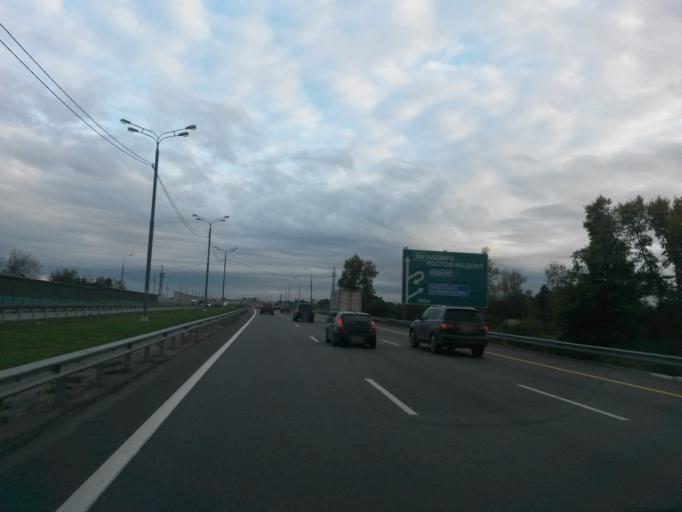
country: RU
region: Moskovskaya
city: Yam
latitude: 55.4883
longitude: 37.7379
